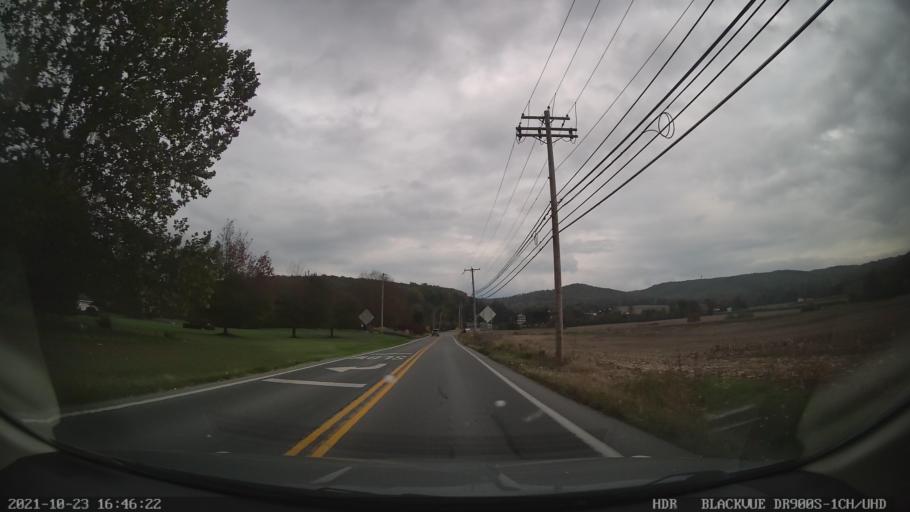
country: US
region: Pennsylvania
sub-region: Berks County
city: Red Lion
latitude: 40.4941
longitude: -75.6509
